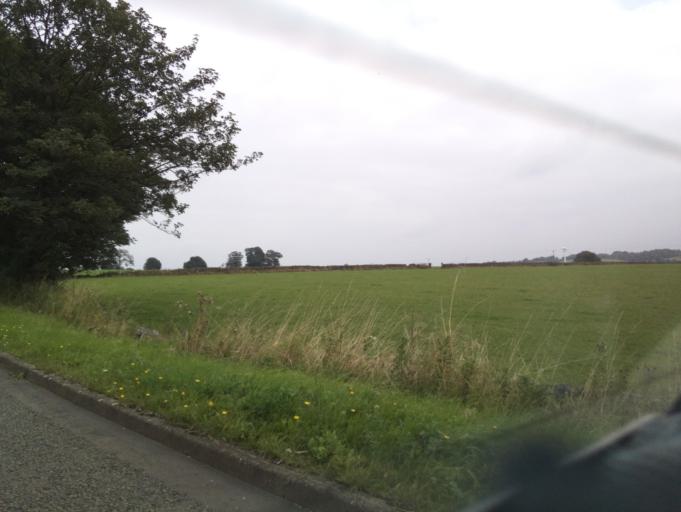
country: GB
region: England
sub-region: Staffordshire
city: Mayfield
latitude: 53.0357
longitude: -1.8274
